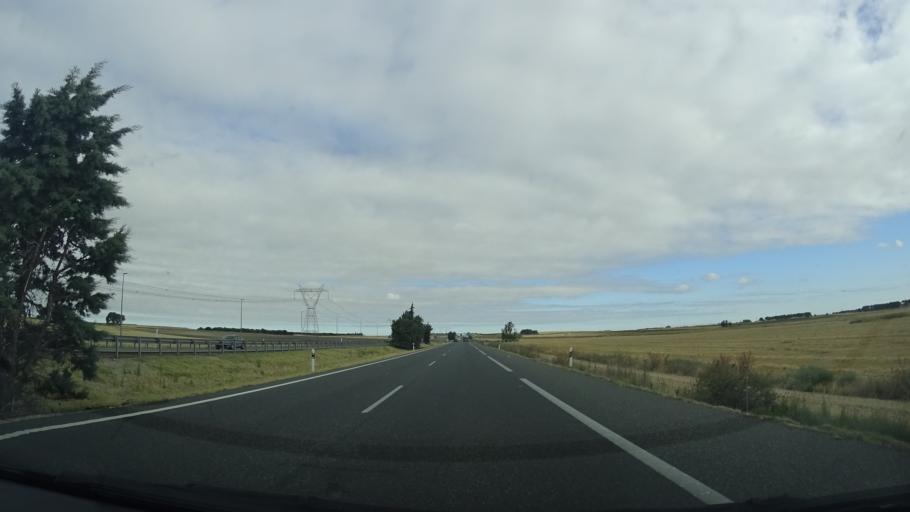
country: ES
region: Castille and Leon
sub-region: Provincia de Avila
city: Palacios de Goda
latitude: 41.1328
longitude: -4.7762
